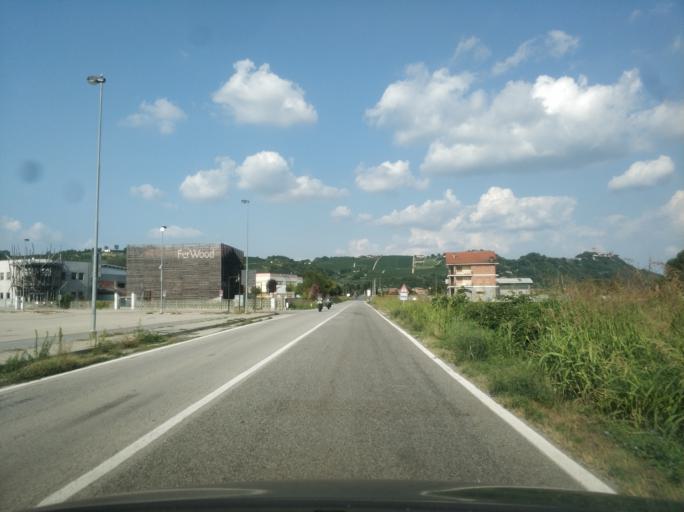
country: IT
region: Piedmont
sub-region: Provincia di Cuneo
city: Cinzano
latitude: 44.6907
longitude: 7.9040
